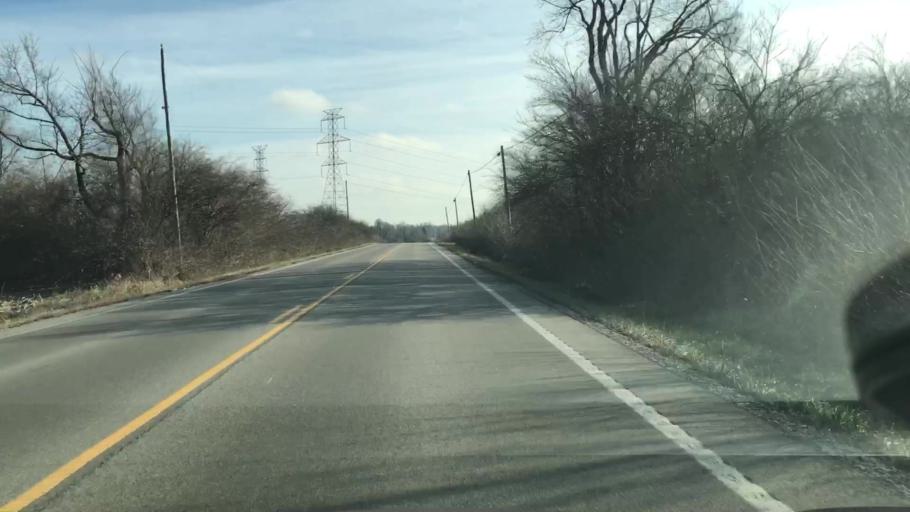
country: US
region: Ohio
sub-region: Greene County
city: Fairborn
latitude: 39.8060
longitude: -83.9757
